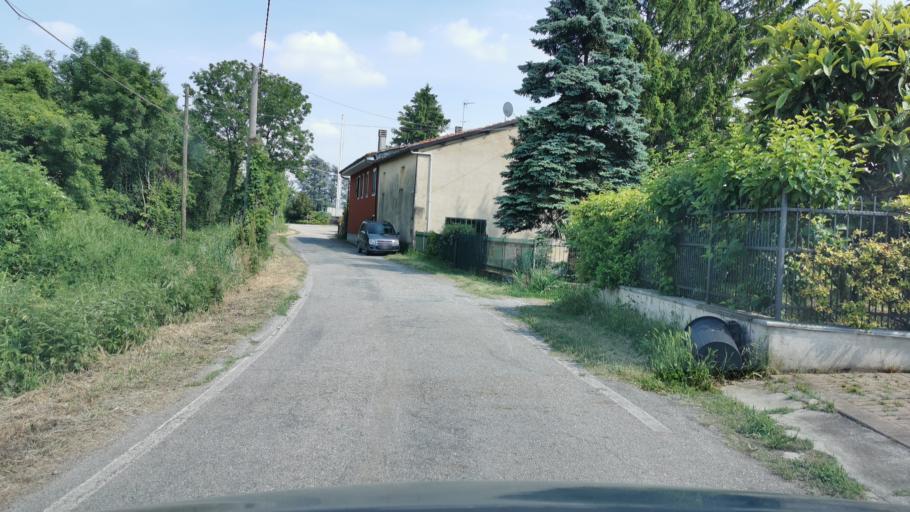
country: IT
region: Piedmont
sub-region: Provincia di Asti
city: Grazzano Badoglio
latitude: 45.0567
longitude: 8.3098
